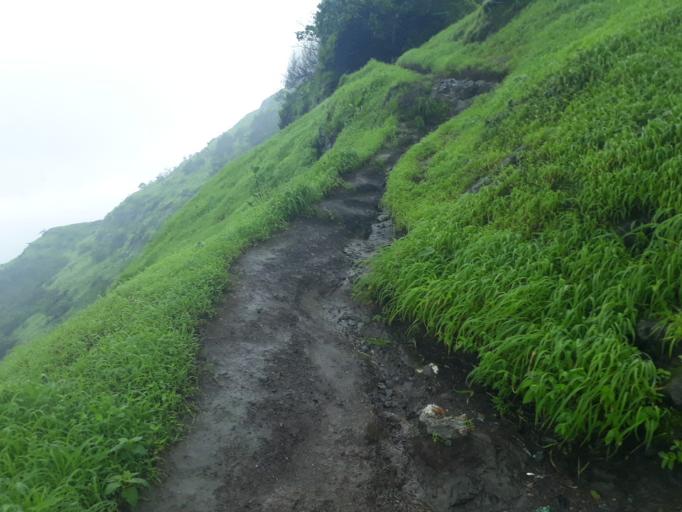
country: IN
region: Maharashtra
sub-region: Pune Division
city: Wadgaon
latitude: 18.6315
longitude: 73.5163
